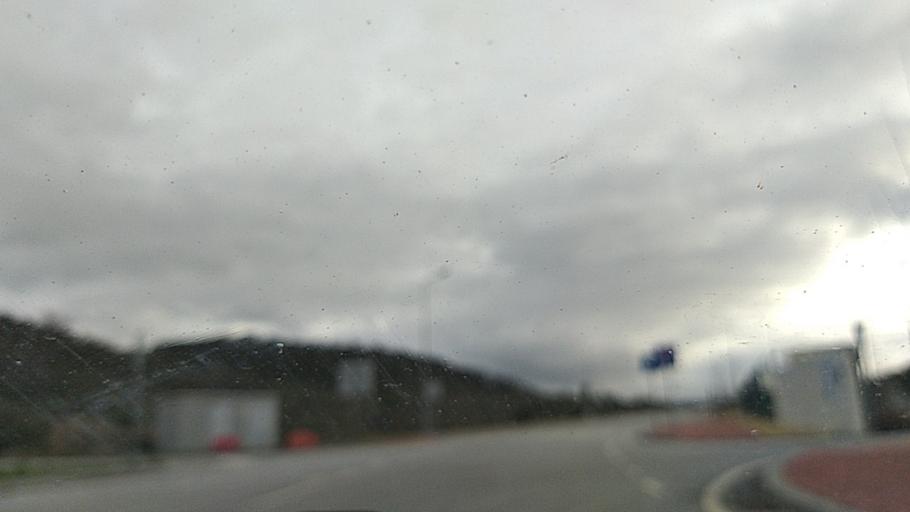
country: PT
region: Guarda
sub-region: Celorico da Beira
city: Celorico da Beira
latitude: 40.6269
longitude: -7.4189
